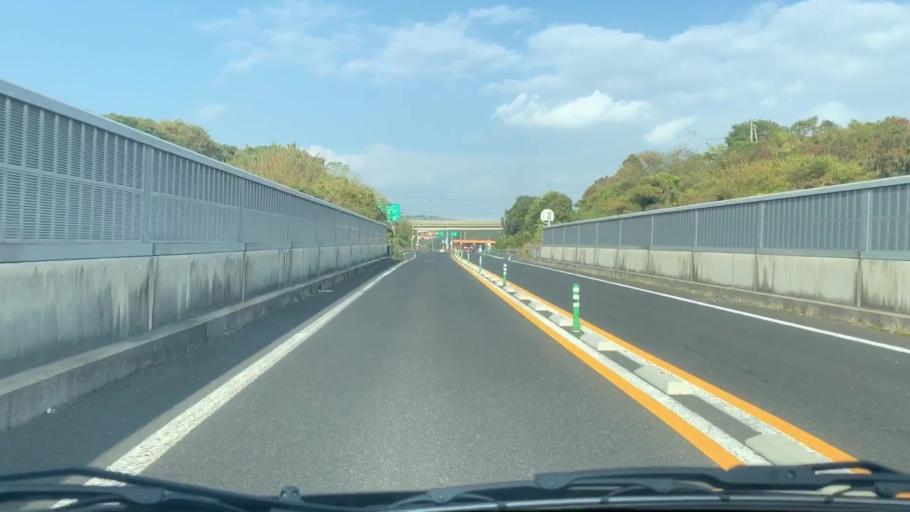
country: JP
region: Nagasaki
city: Sasebo
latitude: 33.0623
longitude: 129.7599
